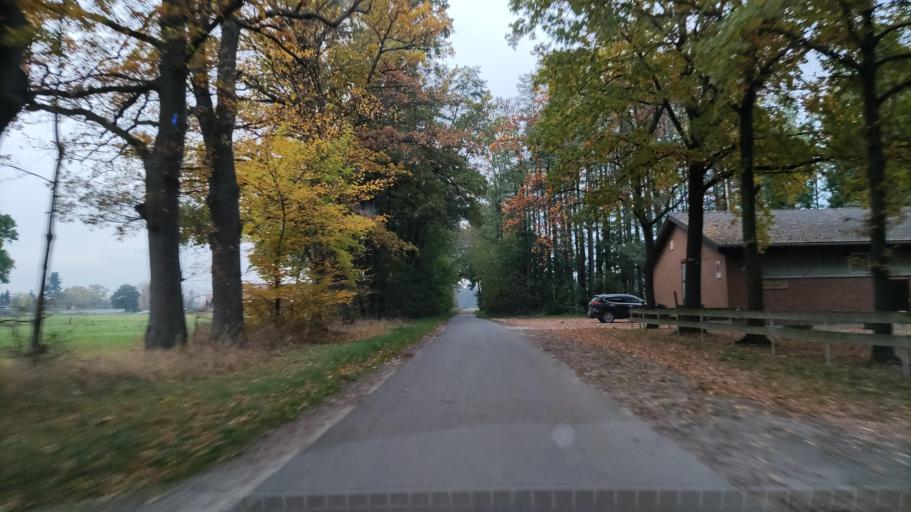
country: DE
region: Saxony-Anhalt
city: Jubar
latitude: 52.6469
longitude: 10.8721
